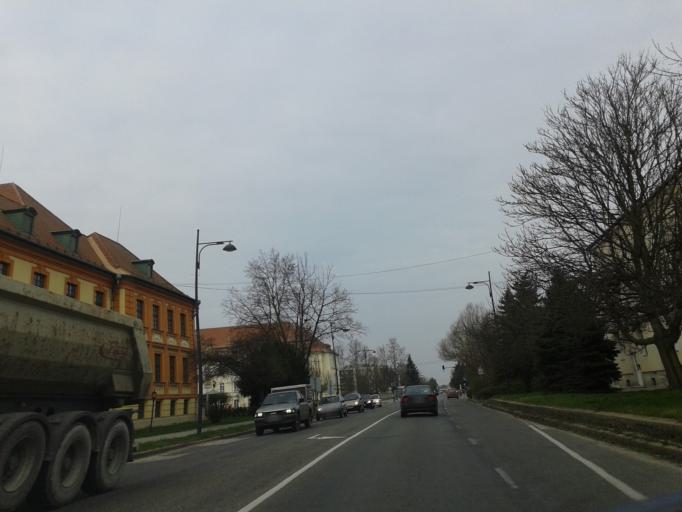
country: HU
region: Komarom-Esztergom
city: Komarom
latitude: 47.7404
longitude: 18.1259
